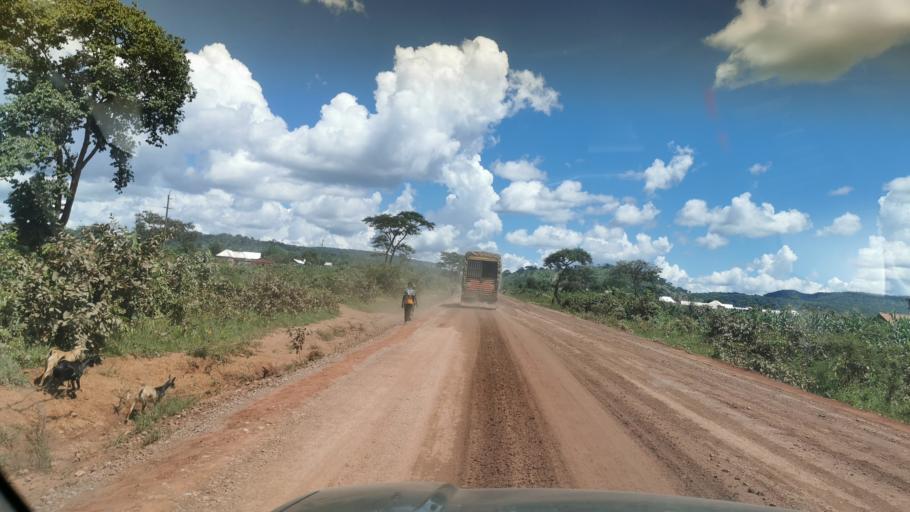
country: TZ
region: Kagera
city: Biharamulo
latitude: -2.8914
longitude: 31.1471
